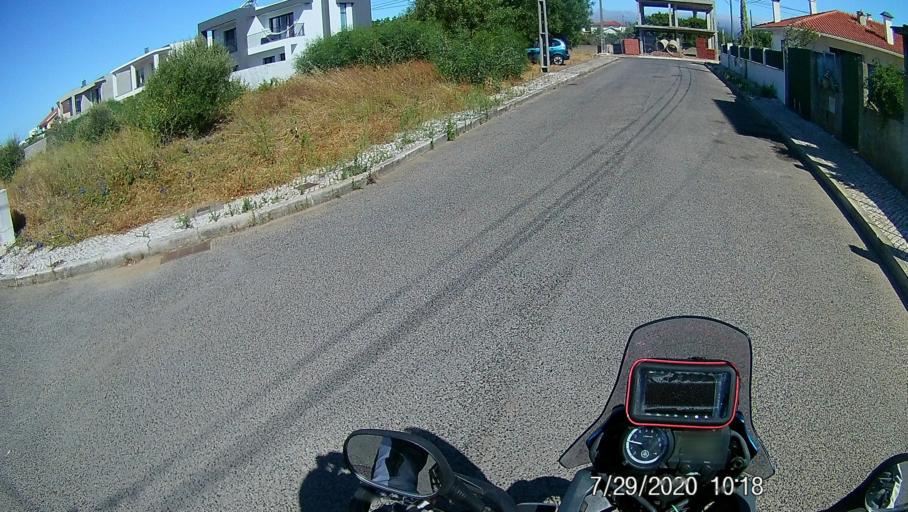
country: PT
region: Lisbon
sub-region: Cascais
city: Estoril
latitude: 38.7239
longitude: -9.3716
